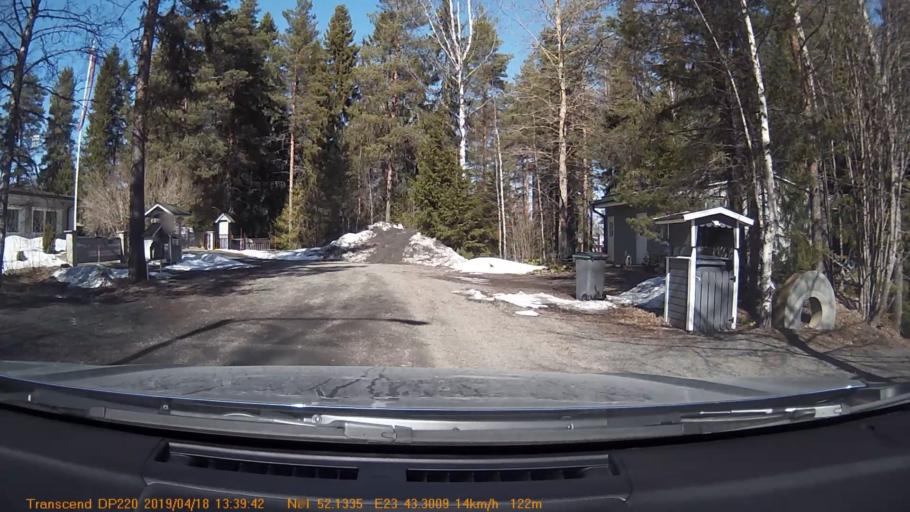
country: FI
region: Pirkanmaa
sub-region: Tampere
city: Kuru
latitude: 61.8692
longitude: 23.7216
